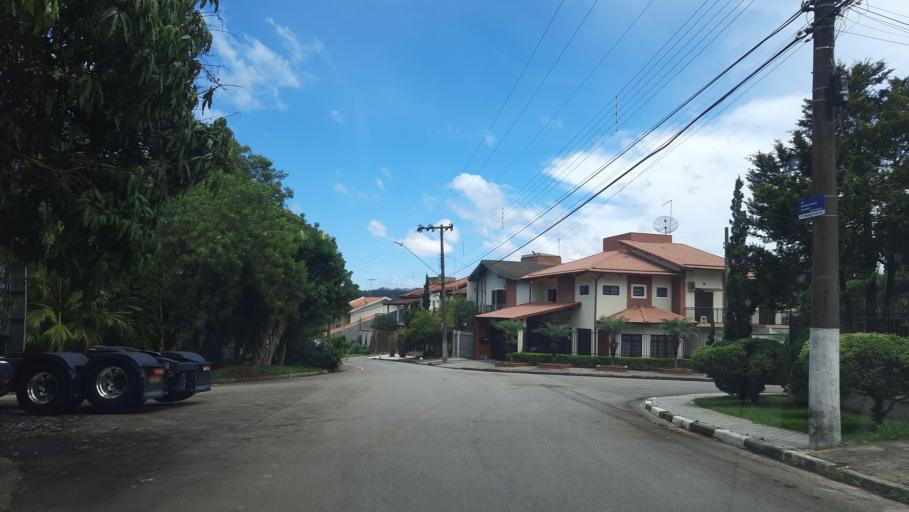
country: BR
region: Sao Paulo
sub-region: Caieiras
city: Caieiras
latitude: -23.3768
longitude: -46.7488
